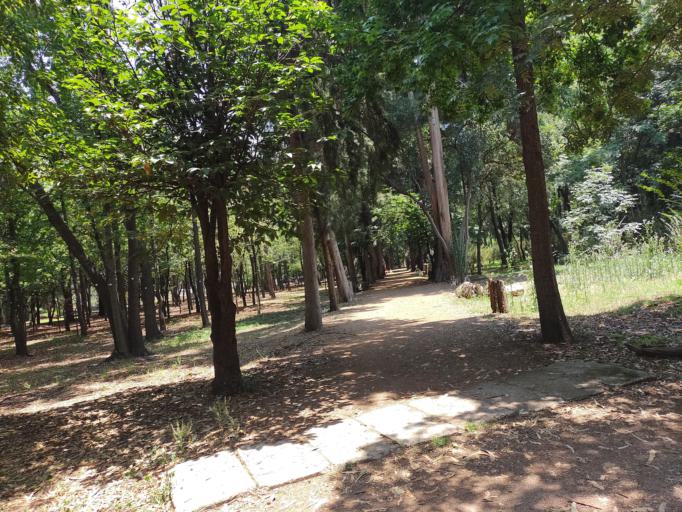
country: MX
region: Mexico City
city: Coyoacan
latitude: 19.3556
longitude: -99.1724
